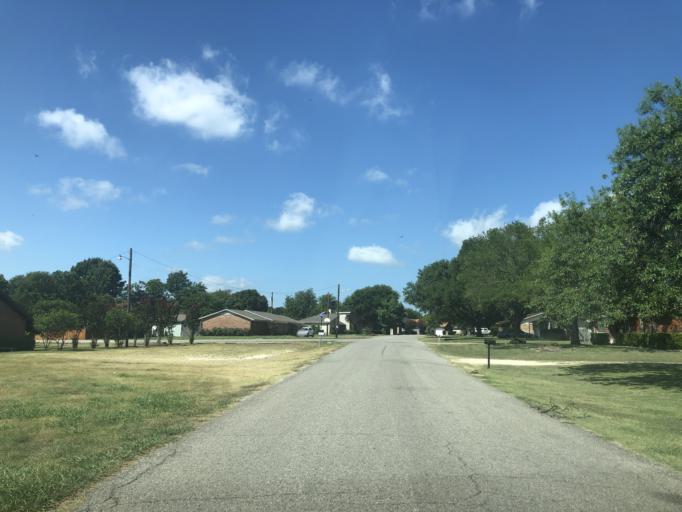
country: US
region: Texas
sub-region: Dallas County
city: Duncanville
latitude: 32.6587
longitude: -96.9217
